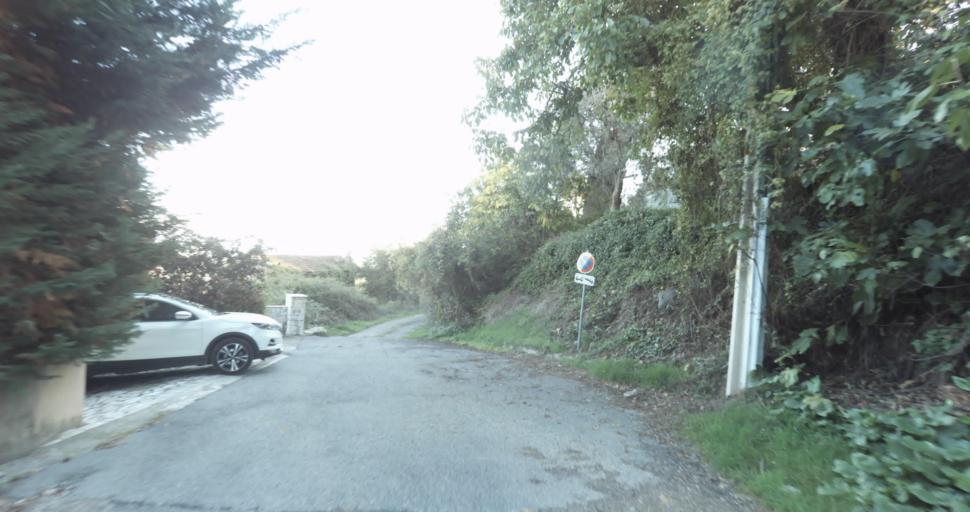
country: FR
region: Provence-Alpes-Cote d'Azur
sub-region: Departement des Alpes-Maritimes
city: Saint-Jeannet
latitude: 43.7412
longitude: 7.1290
